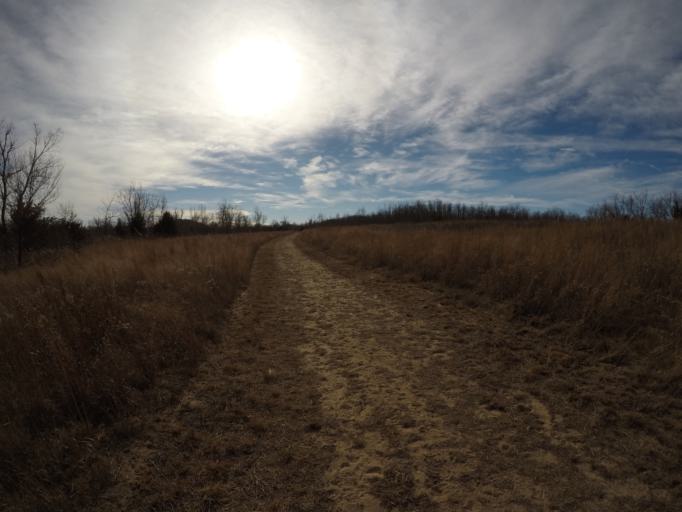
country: US
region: Kansas
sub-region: Reno County
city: Buhler
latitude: 38.1194
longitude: -97.8588
